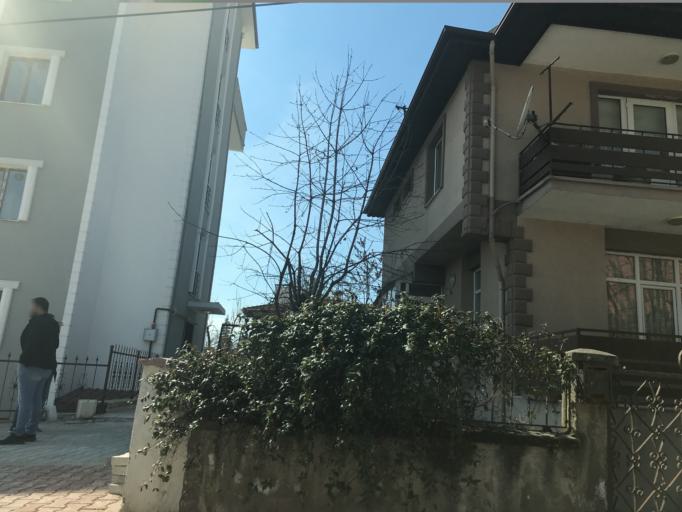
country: TR
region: Karabuk
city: Safranbolu
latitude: 41.2575
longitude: 32.6791
